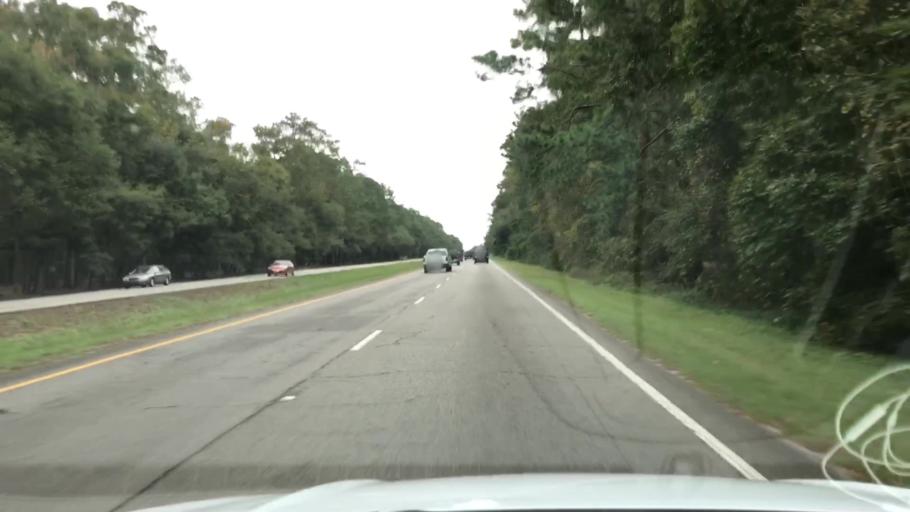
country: US
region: South Carolina
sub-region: Georgetown County
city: Murrells Inlet
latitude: 33.5173
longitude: -79.0706
